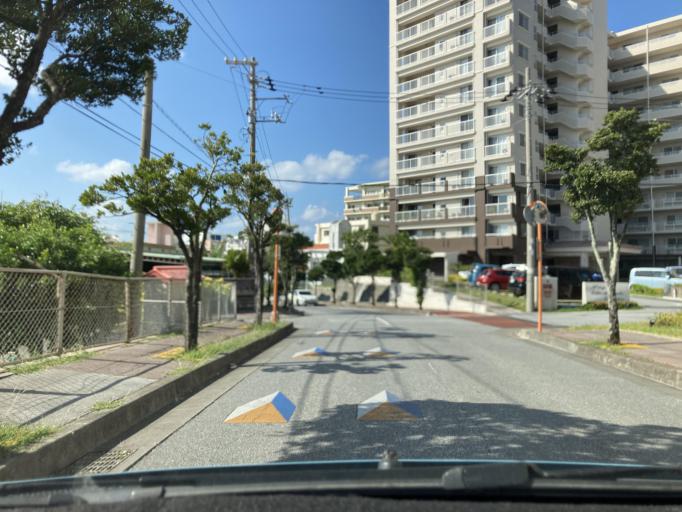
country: JP
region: Okinawa
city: Tomigusuku
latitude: 26.1869
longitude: 127.6576
